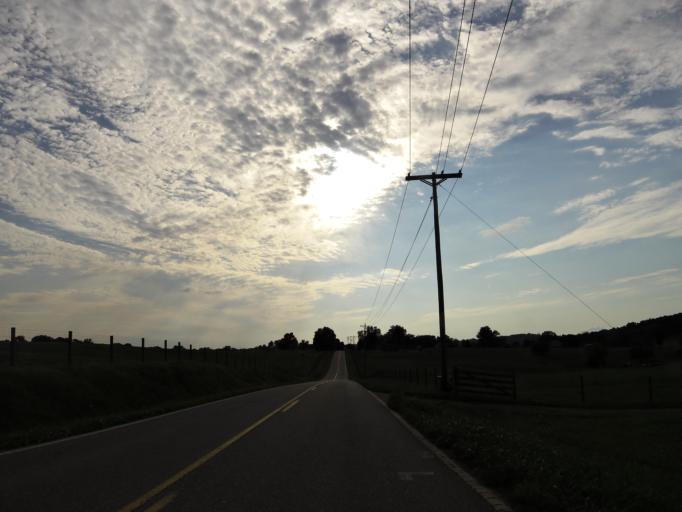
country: US
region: Tennessee
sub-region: Monroe County
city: Vonore
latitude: 35.6112
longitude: -84.2772
